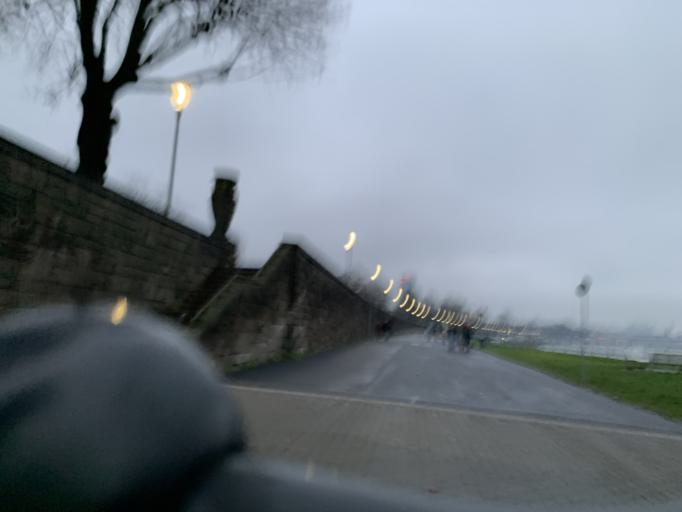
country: DE
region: North Rhine-Westphalia
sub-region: Regierungsbezirk Dusseldorf
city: Dusseldorf
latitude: 51.2451
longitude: 6.7644
